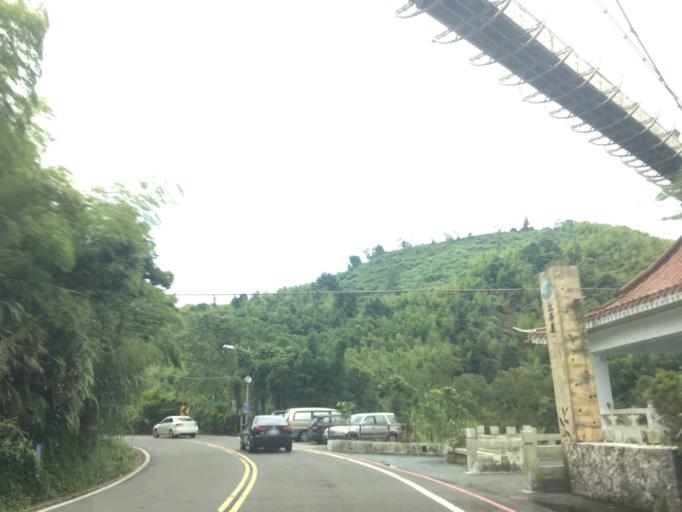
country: TW
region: Taiwan
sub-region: Yunlin
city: Douliu
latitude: 23.5601
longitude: 120.5978
